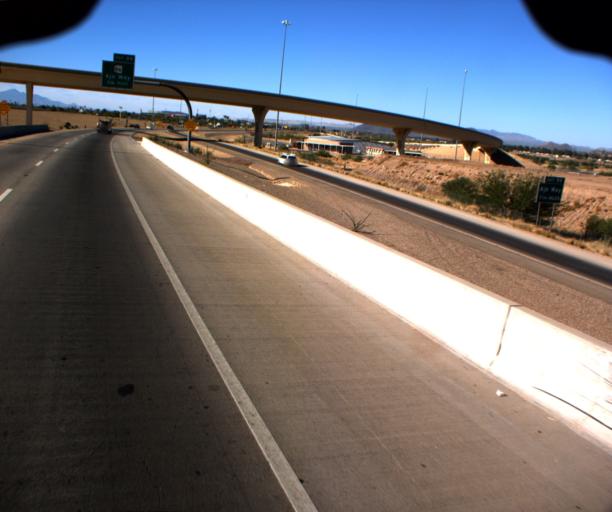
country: US
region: Arizona
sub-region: Pima County
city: South Tucson
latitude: 32.1971
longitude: -110.9792
